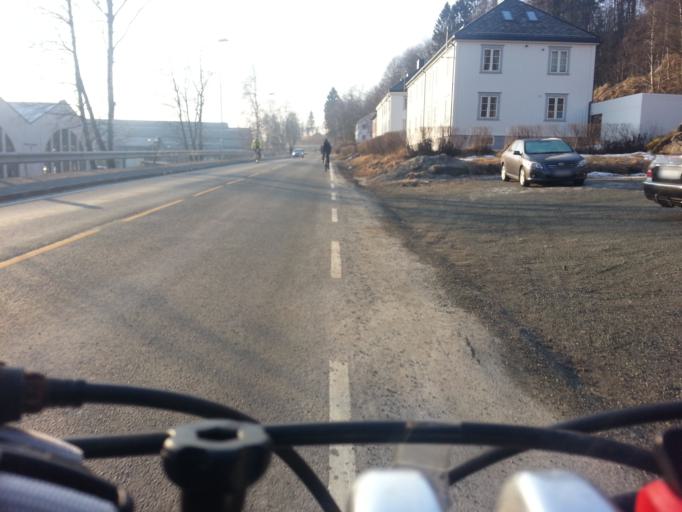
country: NO
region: Sor-Trondelag
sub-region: Trondheim
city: Trondheim
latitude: 63.4193
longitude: 10.3775
